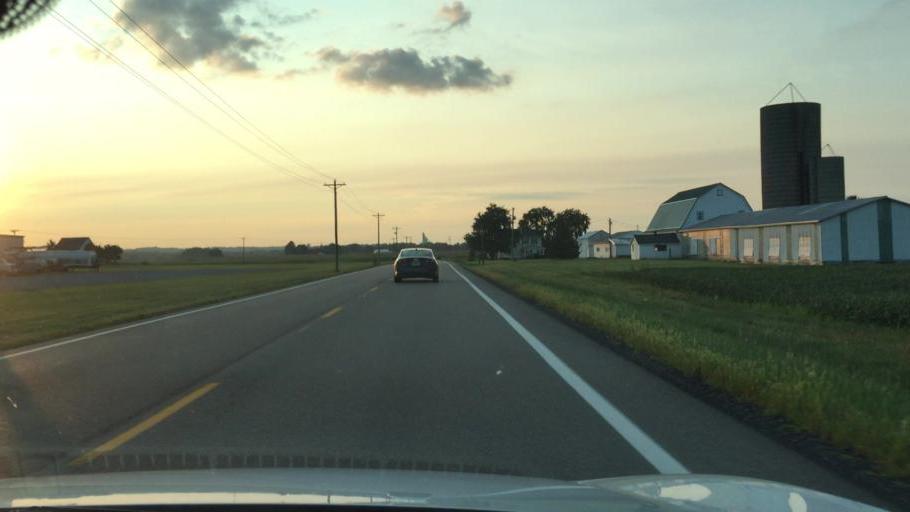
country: US
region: Ohio
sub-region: Champaign County
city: Mechanicsburg
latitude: 40.0560
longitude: -83.5315
